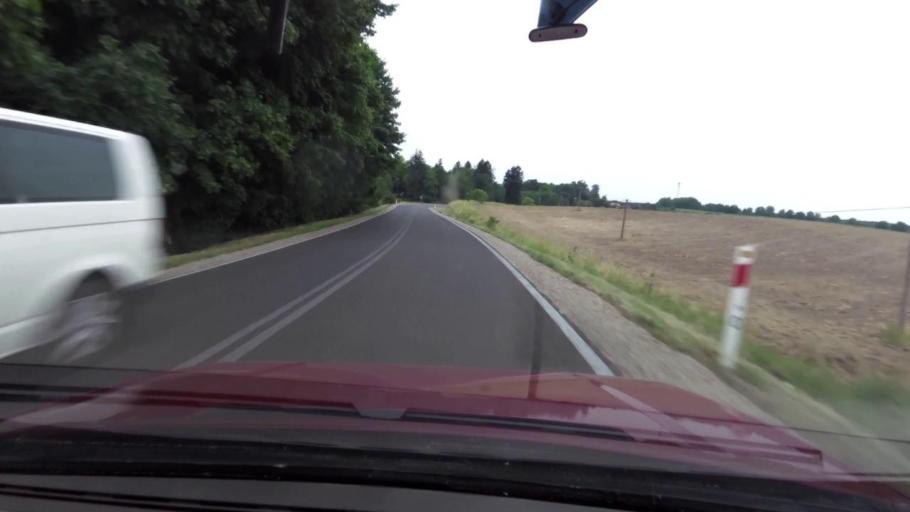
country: PL
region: West Pomeranian Voivodeship
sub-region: Powiat koszalinski
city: Sianow
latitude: 54.1583
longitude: 16.4547
